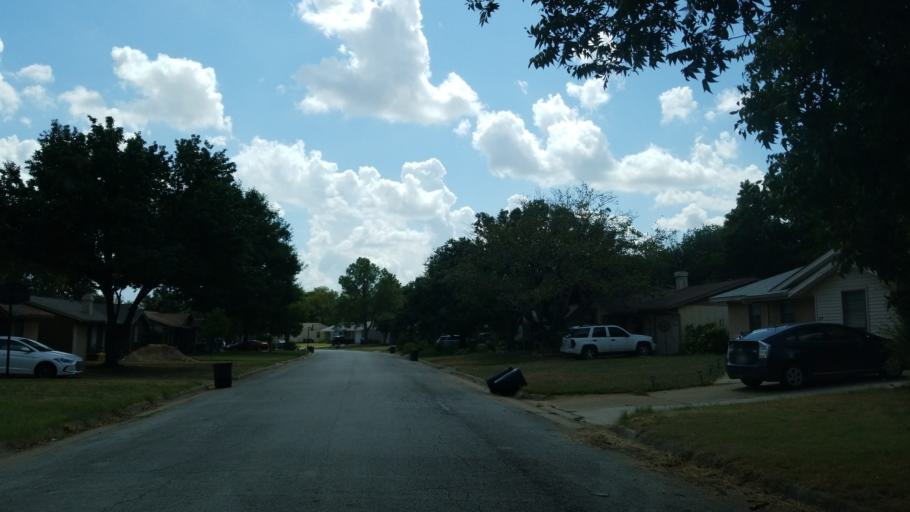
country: US
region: Texas
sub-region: Tarrant County
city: Euless
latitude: 32.8542
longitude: -97.0922
